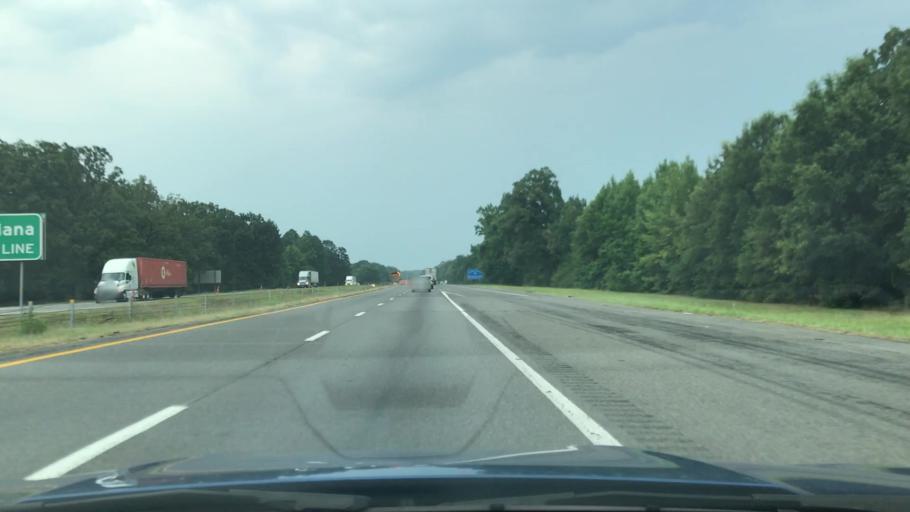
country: US
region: Texas
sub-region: Harrison County
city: Waskom
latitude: 32.4613
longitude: -94.0435
